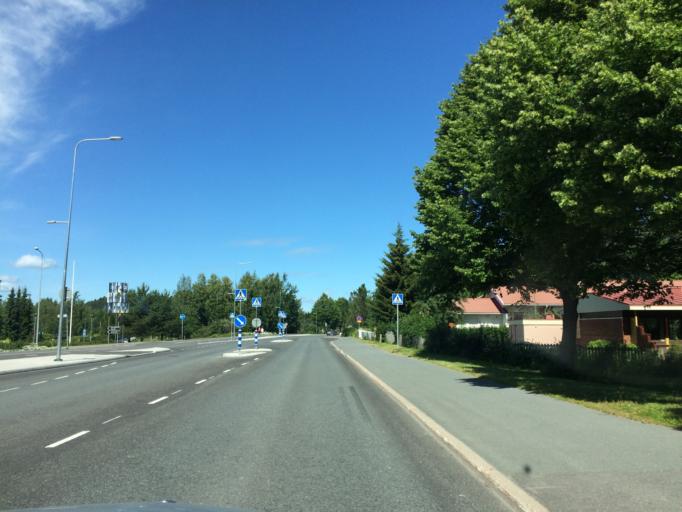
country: FI
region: Haeme
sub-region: Haemeenlinna
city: Haemeenlinna
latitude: 60.9868
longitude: 24.4403
